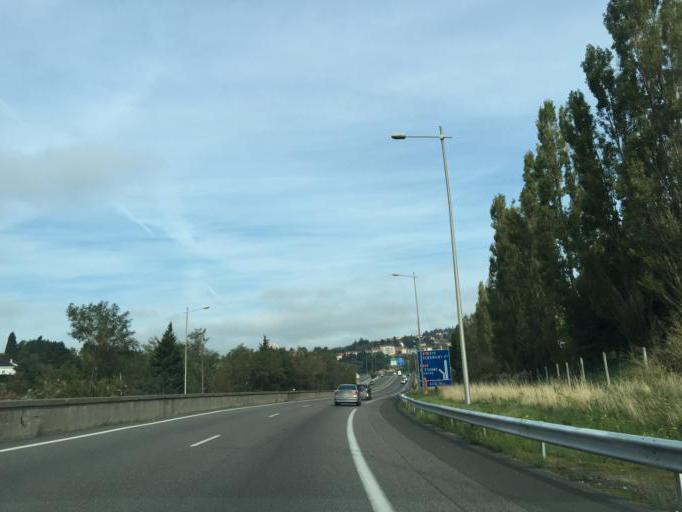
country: FR
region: Rhone-Alpes
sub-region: Departement de la Loire
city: Saint-Jean-Bonnefonds
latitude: 45.4375
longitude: 4.4389
